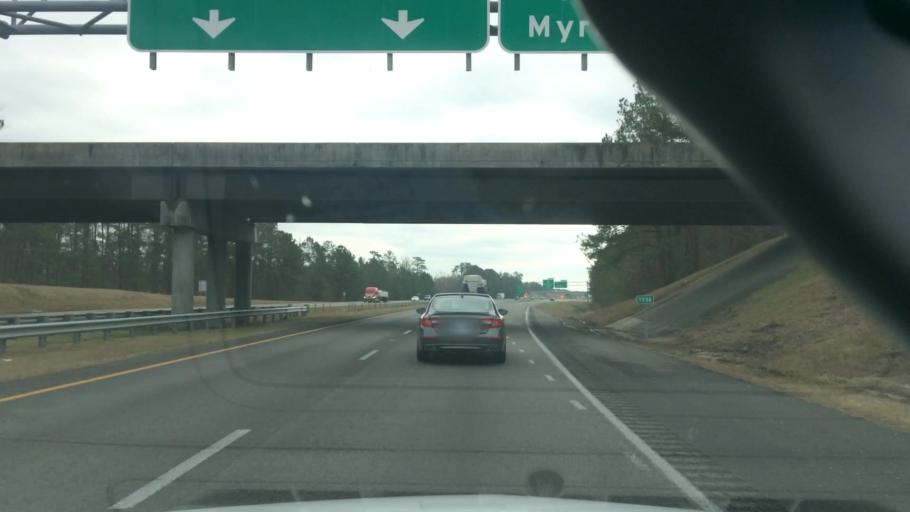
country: US
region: North Carolina
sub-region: New Hanover County
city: Skippers Corner
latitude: 34.3278
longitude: -77.8735
